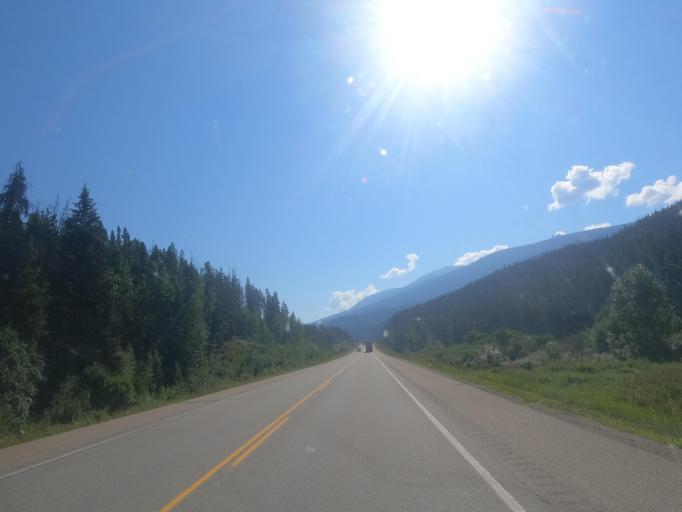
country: CA
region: Alberta
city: Jasper Park Lodge
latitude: 52.8875
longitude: -118.4719
